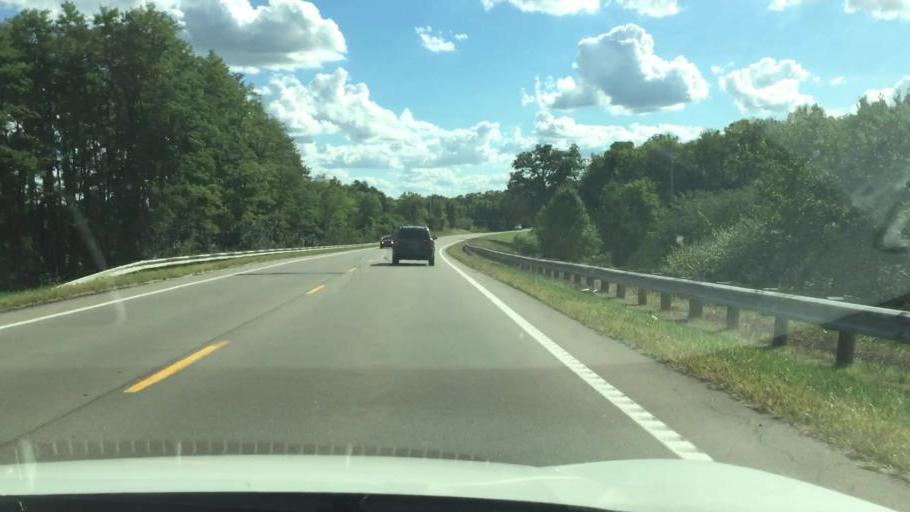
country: US
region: Ohio
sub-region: Clark County
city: Northridge
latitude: 39.9879
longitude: -83.7319
